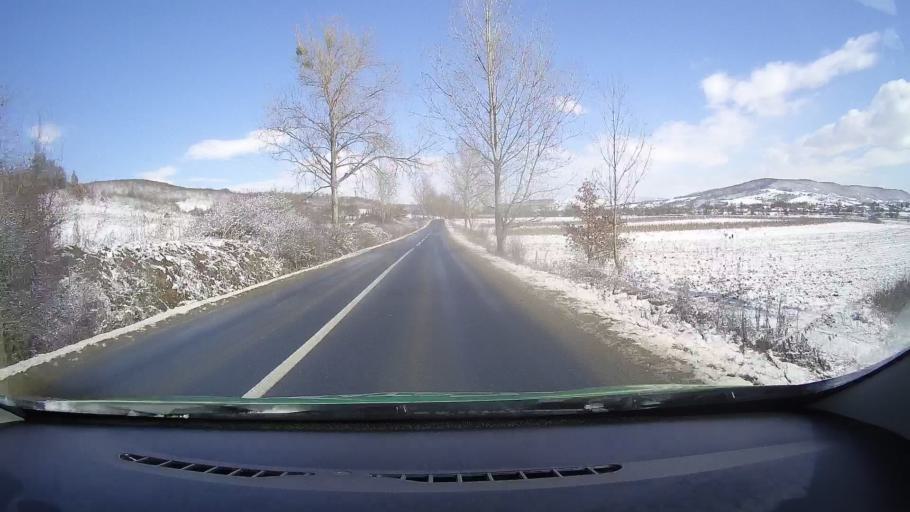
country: RO
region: Sibiu
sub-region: Comuna Nocrich
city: Nocrich
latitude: 45.8385
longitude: 24.4118
